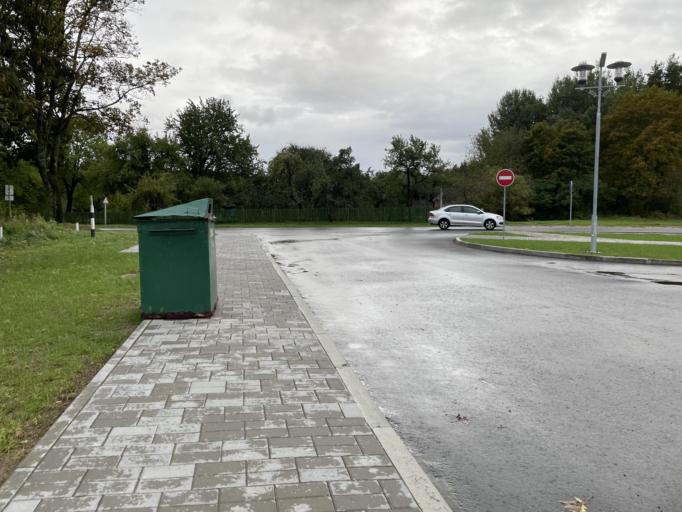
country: BY
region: Brest
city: Kosava
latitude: 52.7659
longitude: 25.1268
